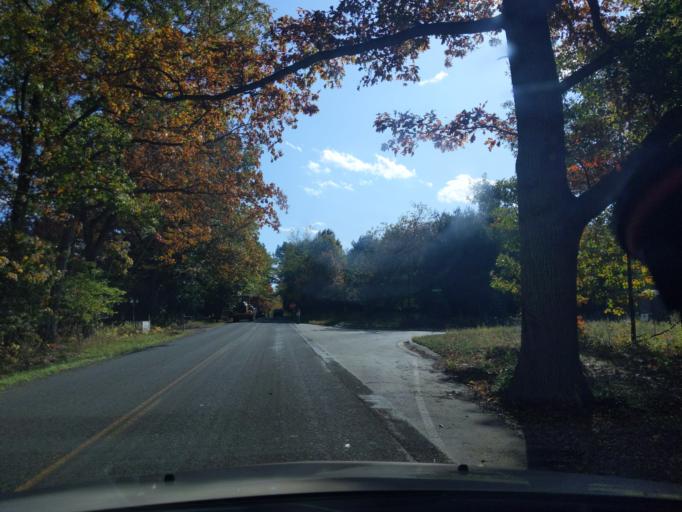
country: US
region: Michigan
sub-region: Ingham County
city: Haslett
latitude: 42.7297
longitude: -84.3930
